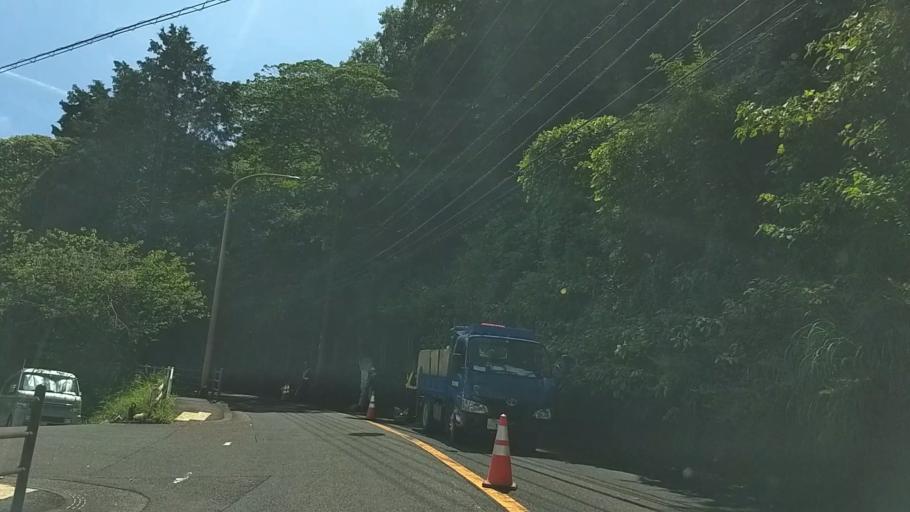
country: JP
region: Kanagawa
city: Zushi
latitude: 35.2934
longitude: 139.5900
